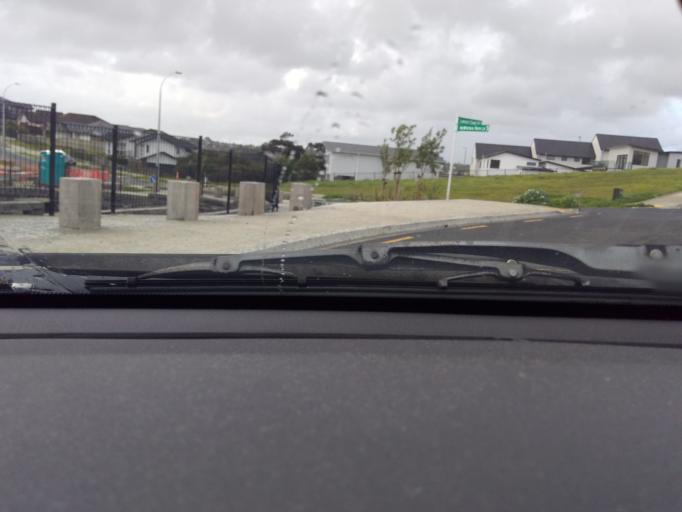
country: NZ
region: Auckland
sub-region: Auckland
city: Rosebank
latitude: -36.8282
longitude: 174.6142
